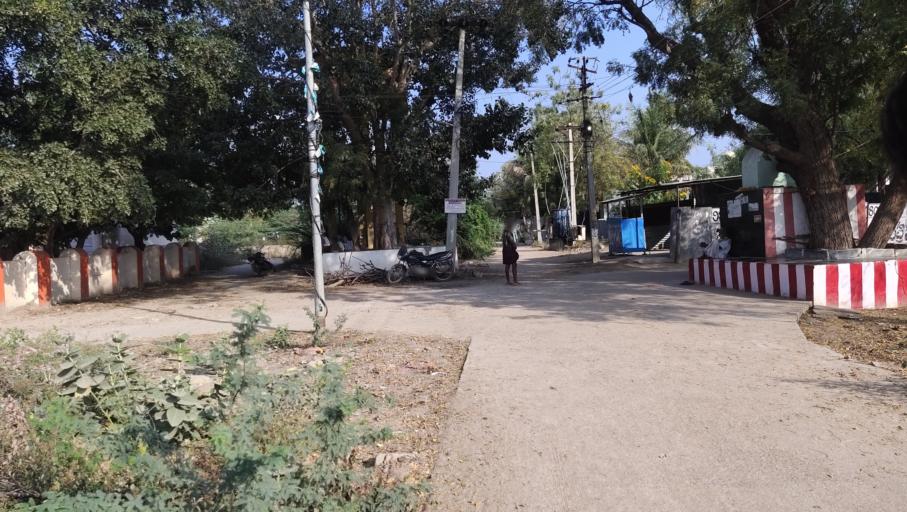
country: IN
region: Andhra Pradesh
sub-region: Anantapur
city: Tadpatri
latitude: 14.9333
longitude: 77.8641
